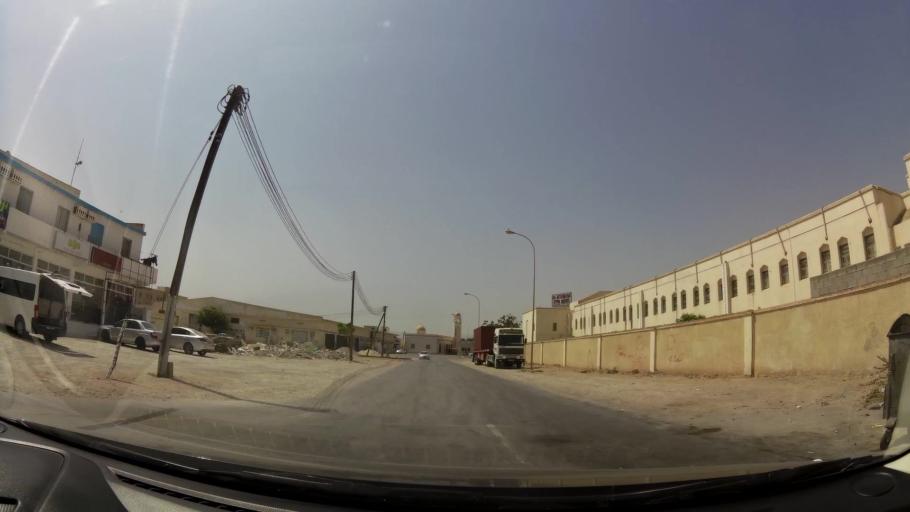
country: OM
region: Zufar
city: Salalah
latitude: 17.0105
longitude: 54.0746
